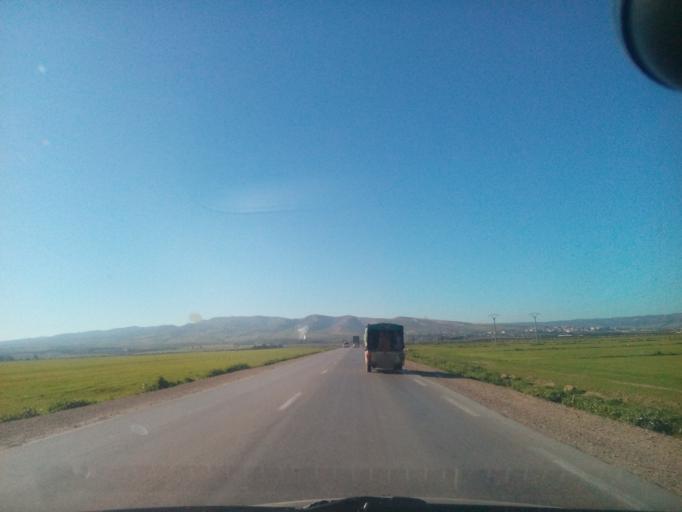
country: DZ
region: Relizane
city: Relizane
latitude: 35.8977
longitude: 0.5551
